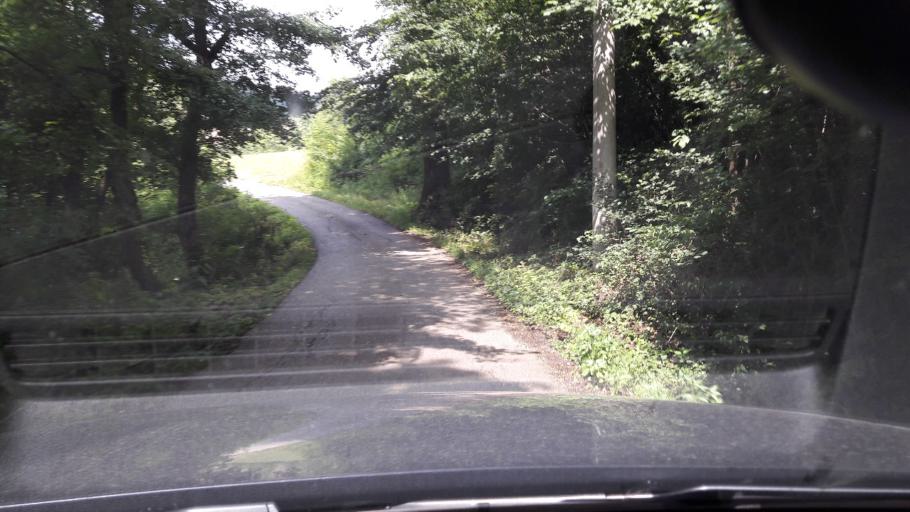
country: RS
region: Central Serbia
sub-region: Belgrade
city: Sopot
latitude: 44.6250
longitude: 20.5995
